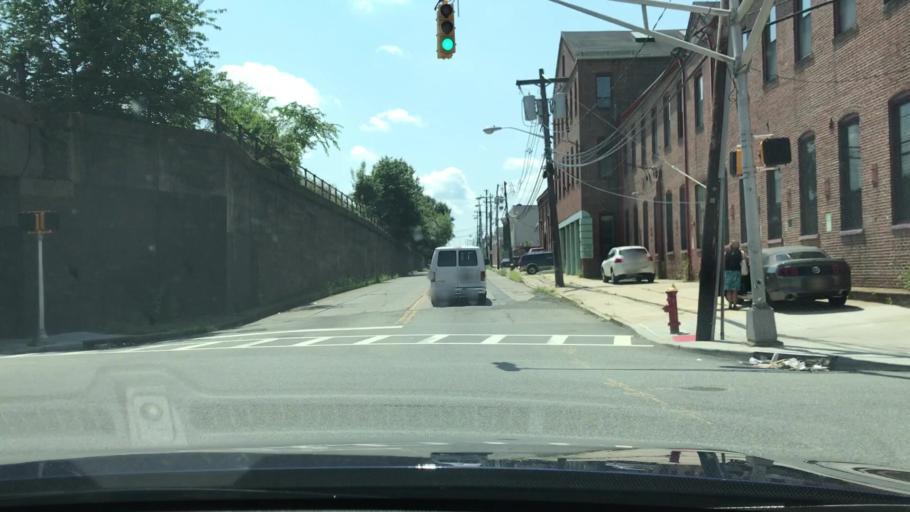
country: US
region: New Jersey
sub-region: Passaic County
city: Paterson
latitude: 40.9131
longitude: -74.1679
